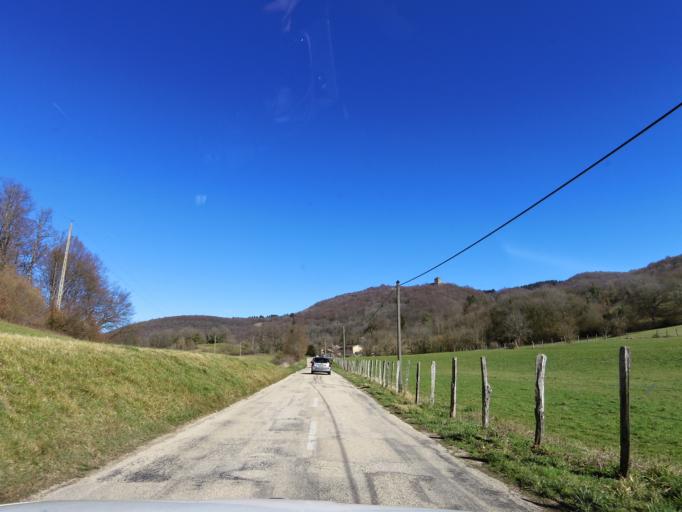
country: FR
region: Rhone-Alpes
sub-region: Departement de l'Ain
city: Ambronay
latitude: 45.9698
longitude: 5.3955
